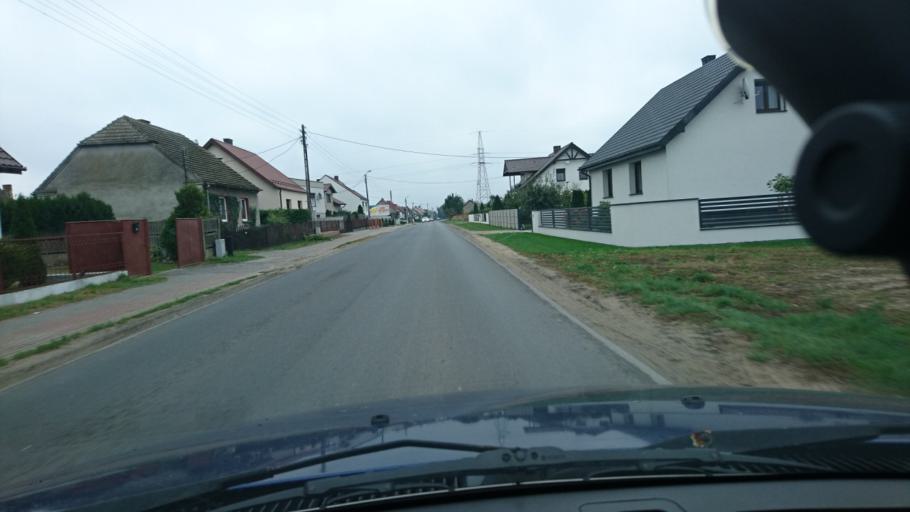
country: PL
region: Greater Poland Voivodeship
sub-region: Powiat ostrowski
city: Odolanow
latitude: 51.5750
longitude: 17.6366
